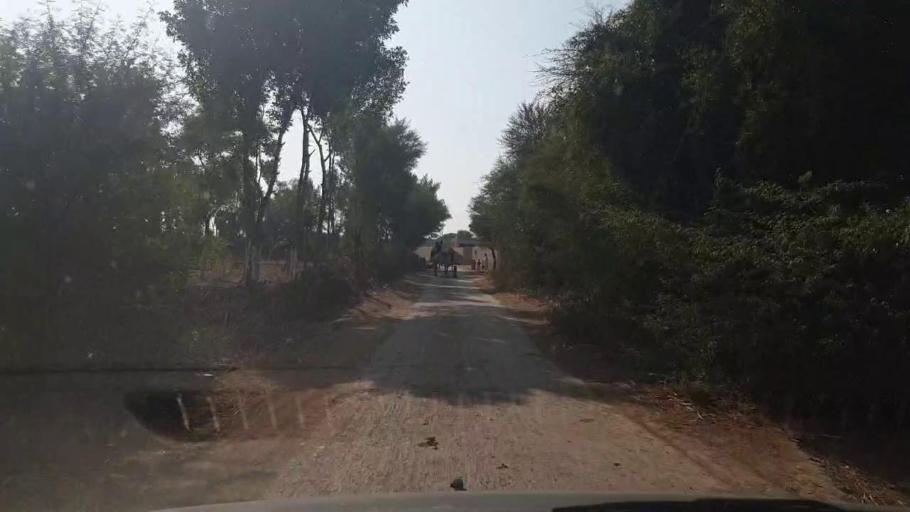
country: PK
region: Sindh
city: Tando Adam
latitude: 25.7528
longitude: 68.6151
